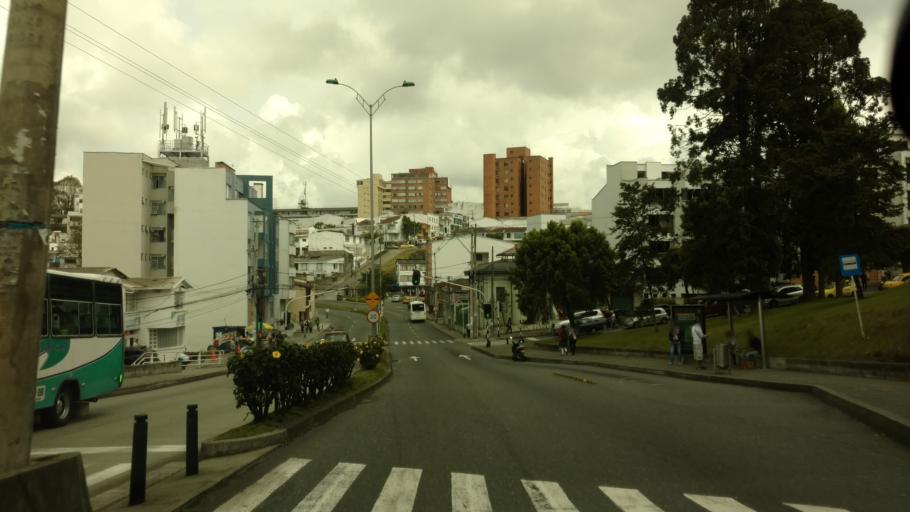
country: CO
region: Caldas
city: Villamaria
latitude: 5.0579
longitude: -75.4908
